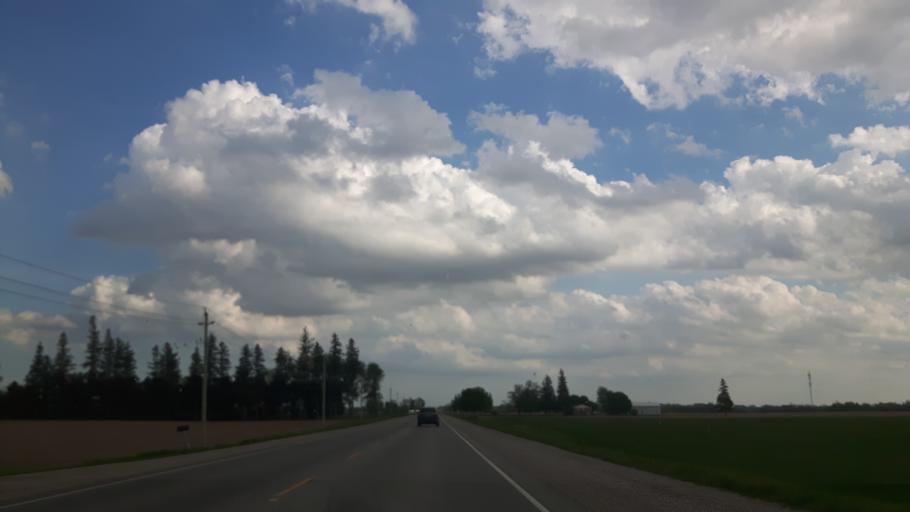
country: CA
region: Ontario
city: South Huron
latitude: 43.3782
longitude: -81.4870
